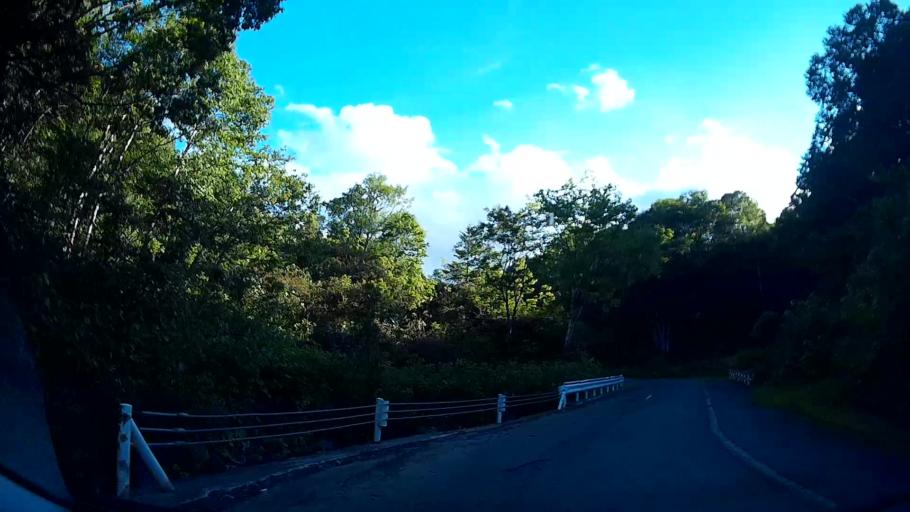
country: JP
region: Hokkaido
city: Otaru
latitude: 42.9808
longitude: 141.0416
